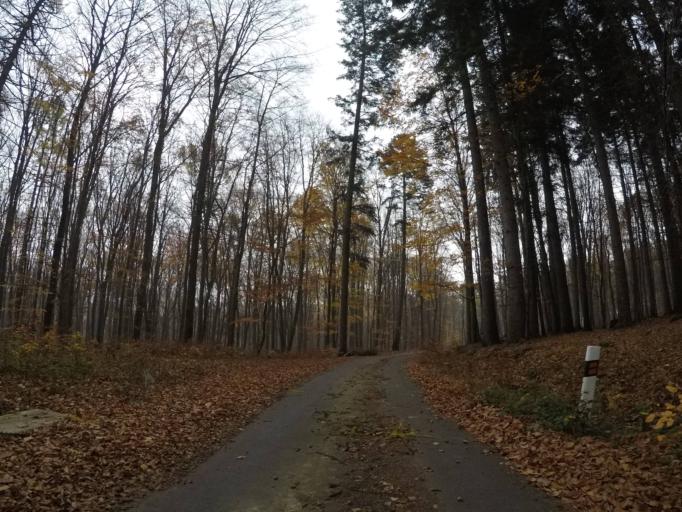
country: SK
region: Presovsky
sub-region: Okres Presov
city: Presov
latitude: 48.8856
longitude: 21.1914
